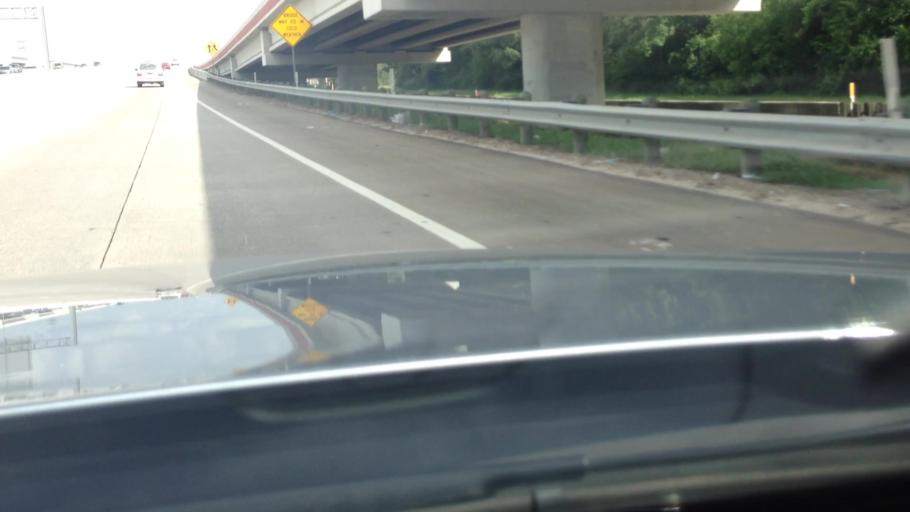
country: US
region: Texas
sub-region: Harris County
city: Hudson
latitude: 29.9421
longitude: -95.5227
